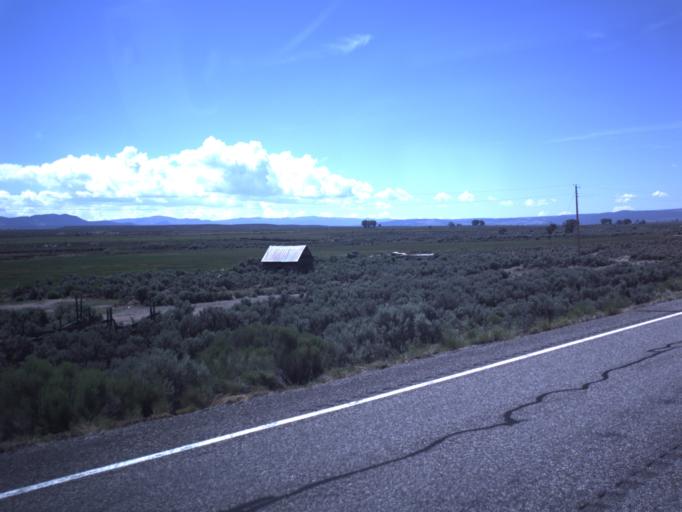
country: US
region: Utah
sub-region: Garfield County
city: Panguitch
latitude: 37.9749
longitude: -112.4057
